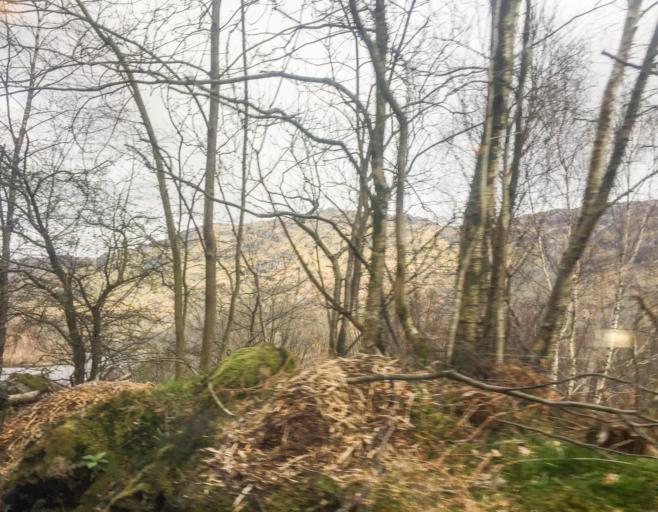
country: GB
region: Scotland
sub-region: Argyll and Bute
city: Garelochhead
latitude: 56.2732
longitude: -4.7070
